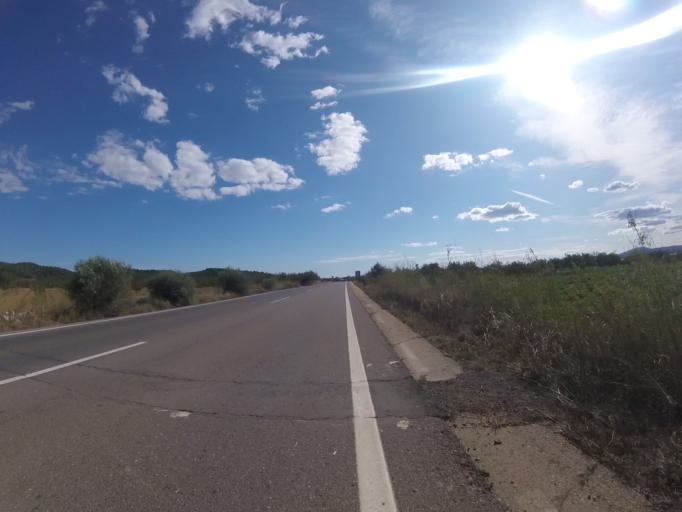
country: ES
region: Valencia
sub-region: Provincia de Castello
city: Alcala de Xivert
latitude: 40.2608
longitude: 0.2436
